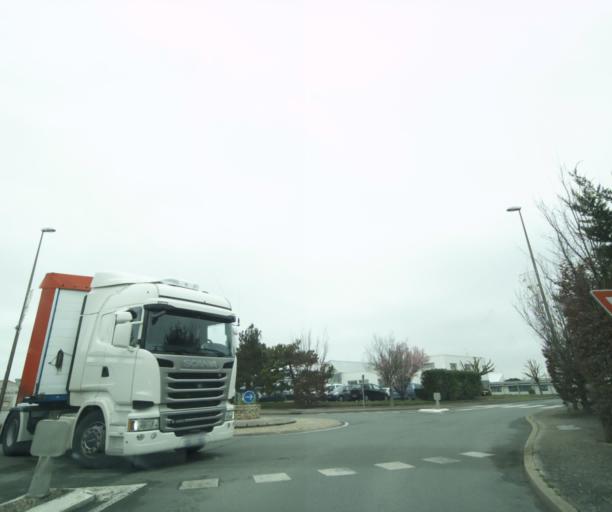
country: FR
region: Poitou-Charentes
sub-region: Departement de la Charente-Maritime
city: Lagord
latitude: 46.1849
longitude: -1.1445
